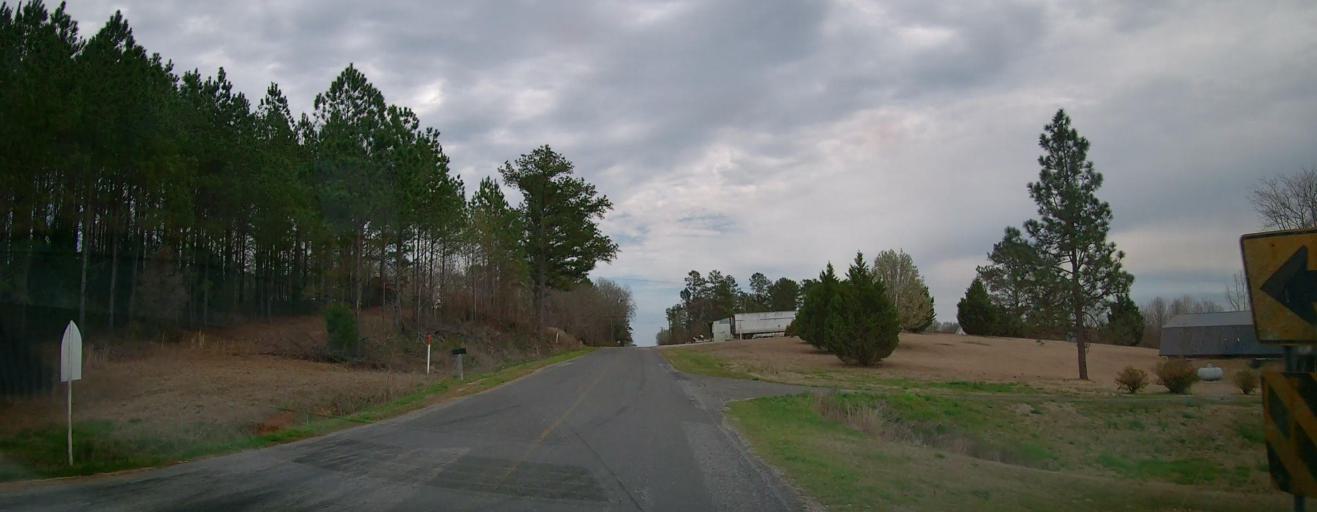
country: US
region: Alabama
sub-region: Marion County
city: Hamilton
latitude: 34.1900
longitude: -88.1481
